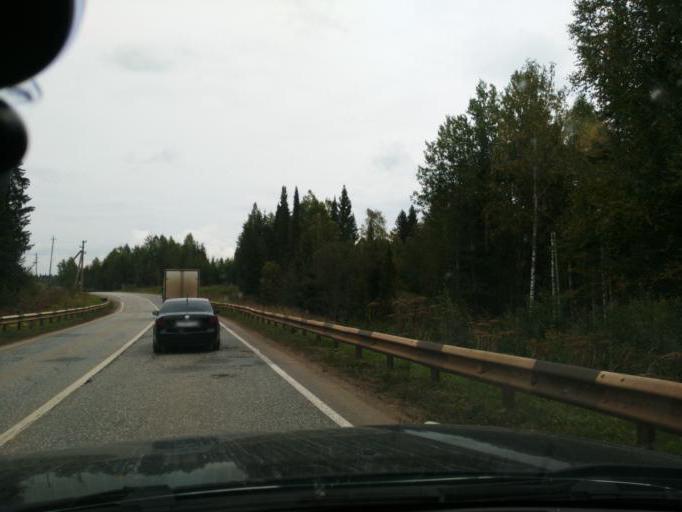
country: RU
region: Bashkortostan
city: Verkhniye Tatyshly
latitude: 56.5001
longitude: 55.8620
